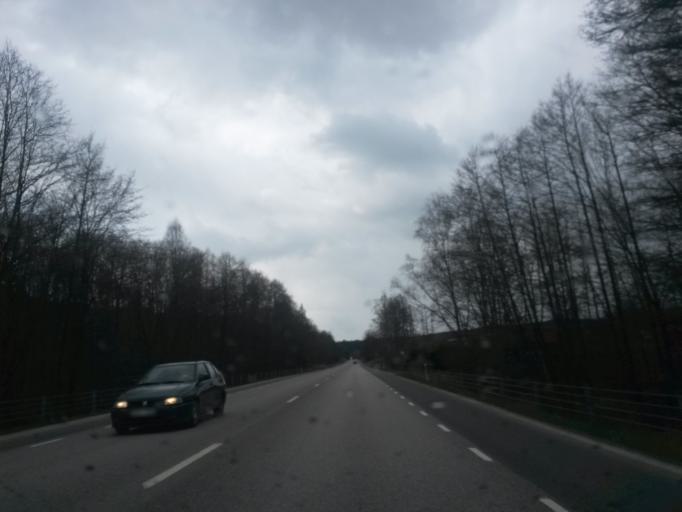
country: SE
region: Vaestra Goetaland
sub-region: Skovde Kommun
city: Skoevde
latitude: 58.3858
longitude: 13.8005
